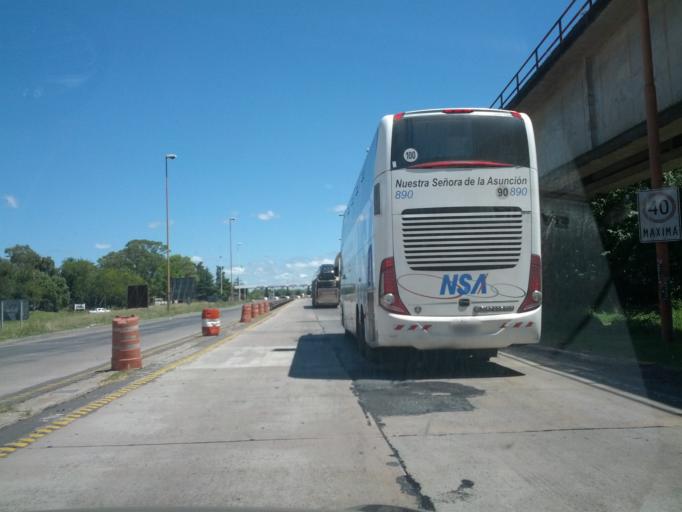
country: AR
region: Buenos Aires
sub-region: Partido de Zarate
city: Zarate
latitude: -34.1160
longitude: -59.0090
